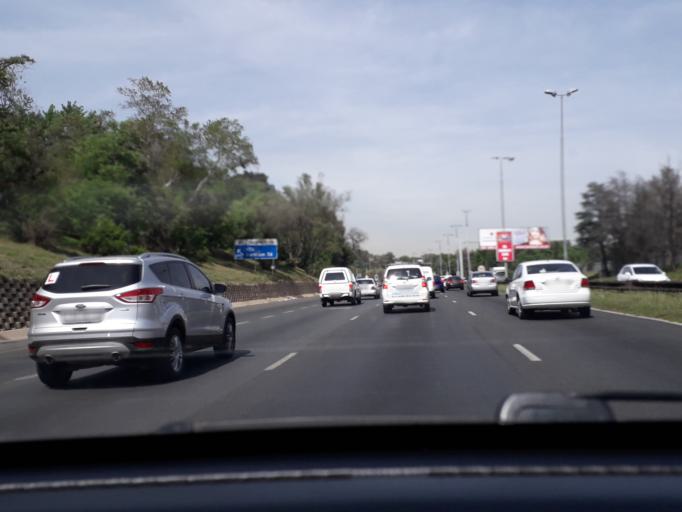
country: ZA
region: Gauteng
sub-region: City of Johannesburg Metropolitan Municipality
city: Johannesburg
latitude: -26.1430
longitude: 28.0619
